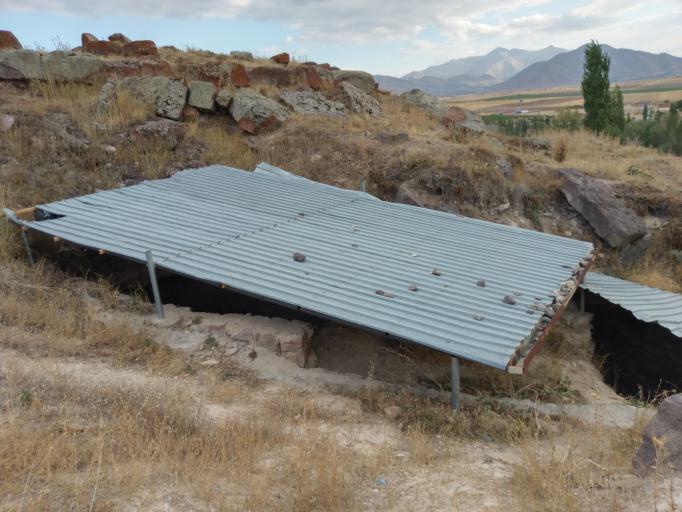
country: TR
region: Kayseri
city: Toklar
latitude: 38.4640
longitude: 36.0795
